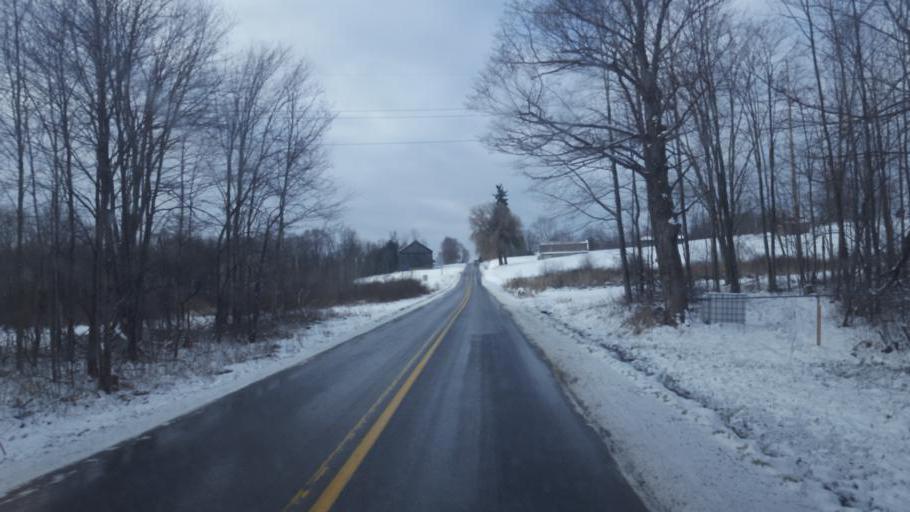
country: US
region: Pennsylvania
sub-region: Mercer County
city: Mercer
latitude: 41.1718
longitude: -80.2484
